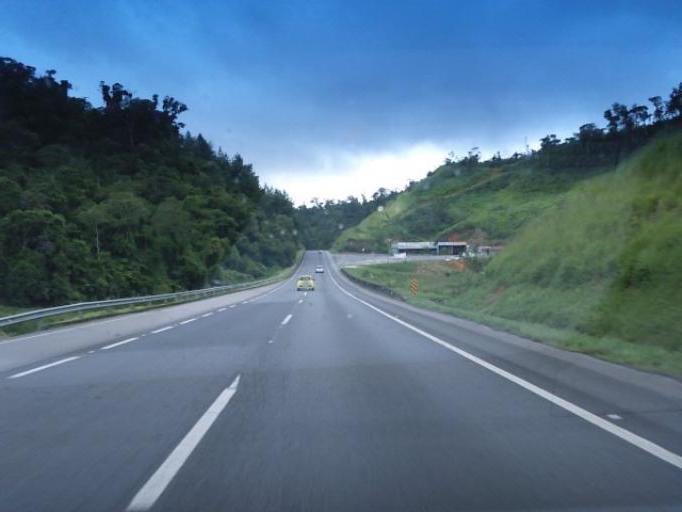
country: BR
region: Parana
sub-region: Antonina
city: Antonina
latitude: -25.0659
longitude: -48.5705
